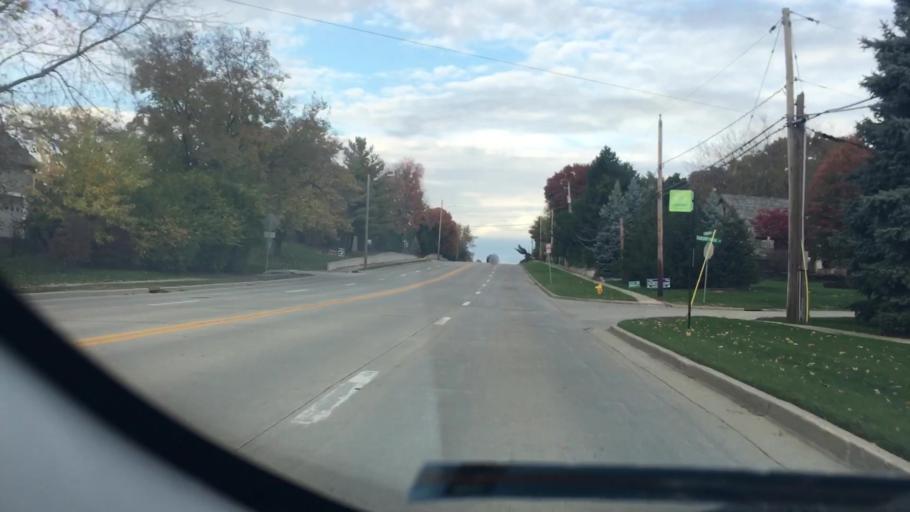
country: US
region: Illinois
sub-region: McLean County
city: Bloomington
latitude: 40.4956
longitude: -88.9628
